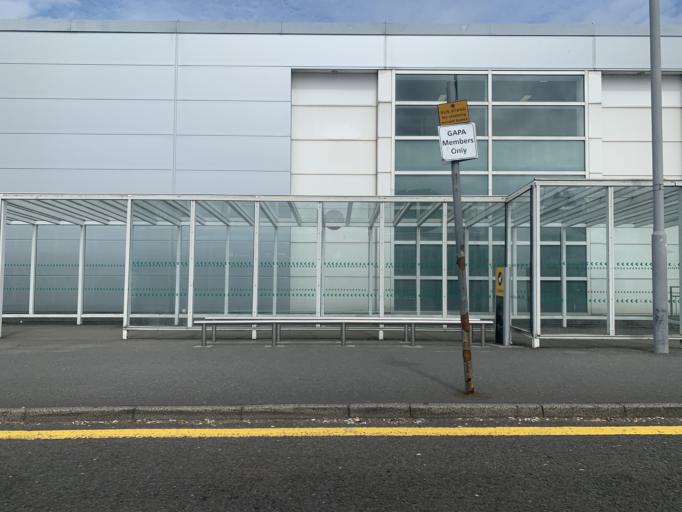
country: GB
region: Scotland
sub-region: Renfrewshire
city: Inchinnan
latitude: 55.8641
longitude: -4.4351
